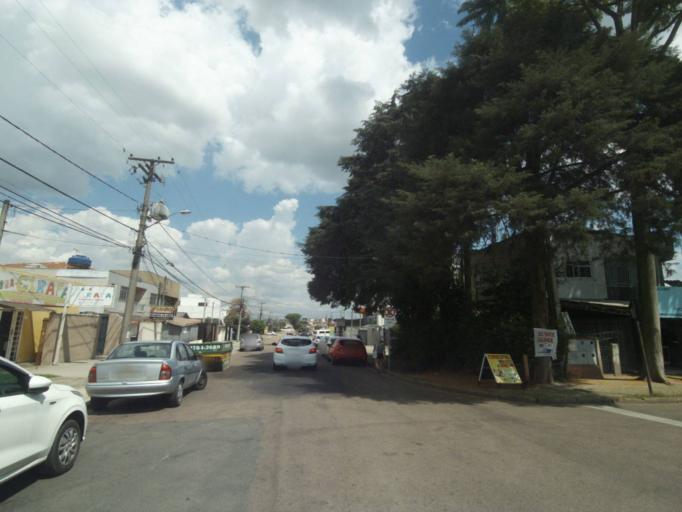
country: BR
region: Parana
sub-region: Sao Jose Dos Pinhais
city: Sao Jose dos Pinhais
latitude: -25.5368
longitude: -49.2712
